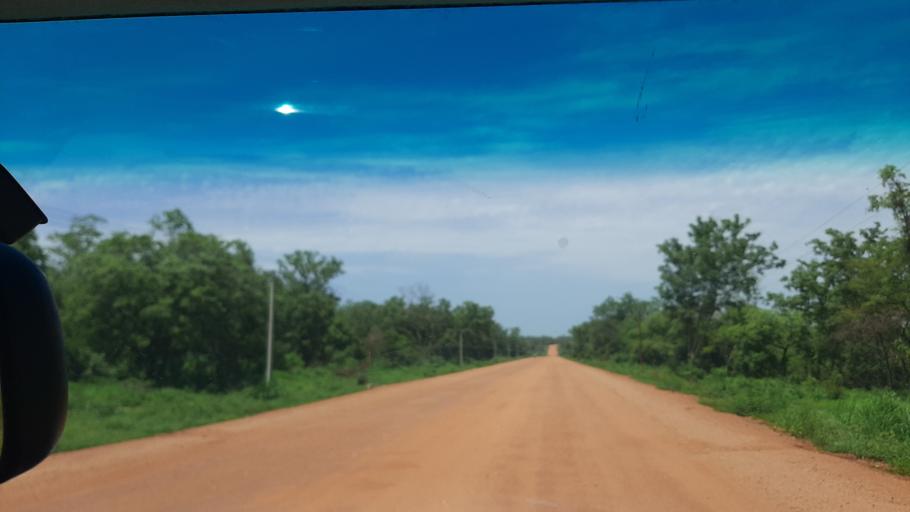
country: ET
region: Gambela
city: Gambela
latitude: 8.0971
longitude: 34.5877
